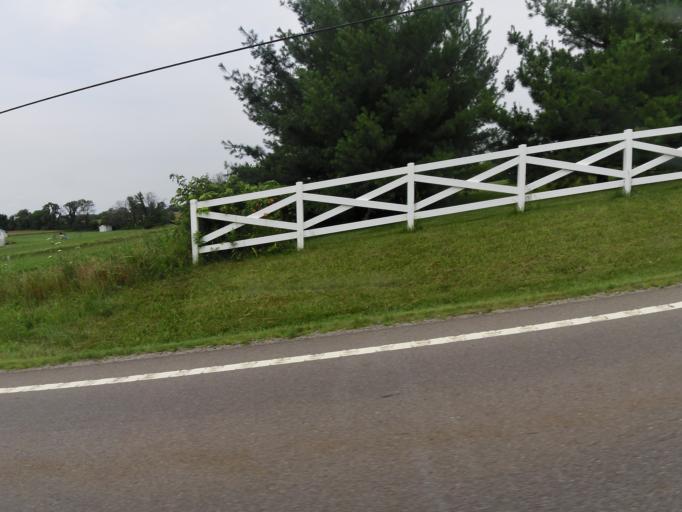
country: US
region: Ohio
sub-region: Warren County
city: Waynesville
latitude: 39.4980
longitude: -83.9895
